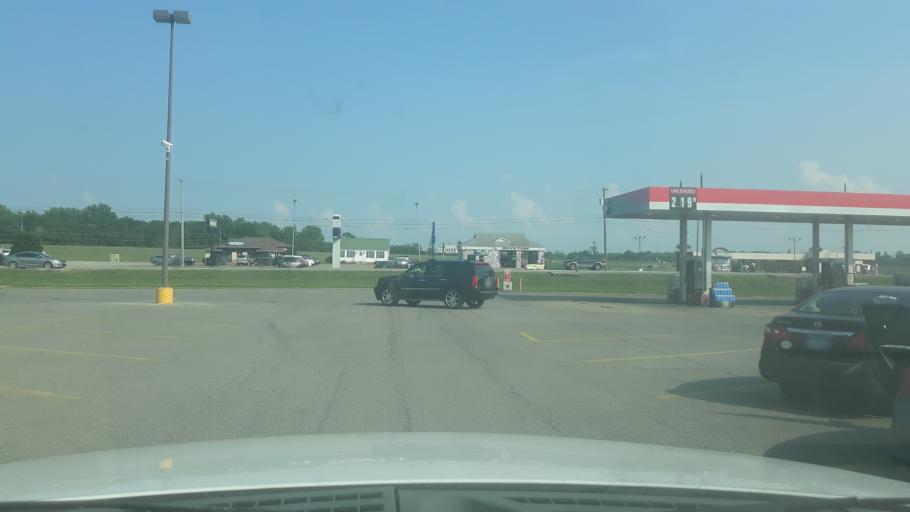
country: US
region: Illinois
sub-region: Saline County
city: Harrisburg
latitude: 37.7450
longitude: -88.5255
